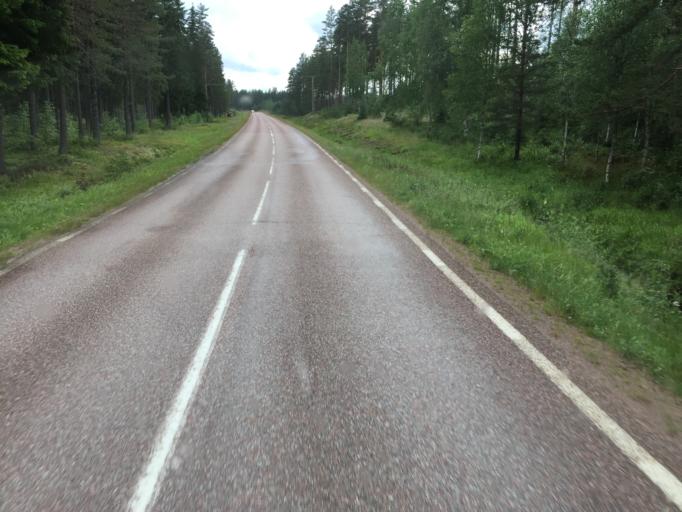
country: SE
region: Dalarna
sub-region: Vansbro Kommun
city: Vansbro
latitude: 60.7274
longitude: 14.1111
